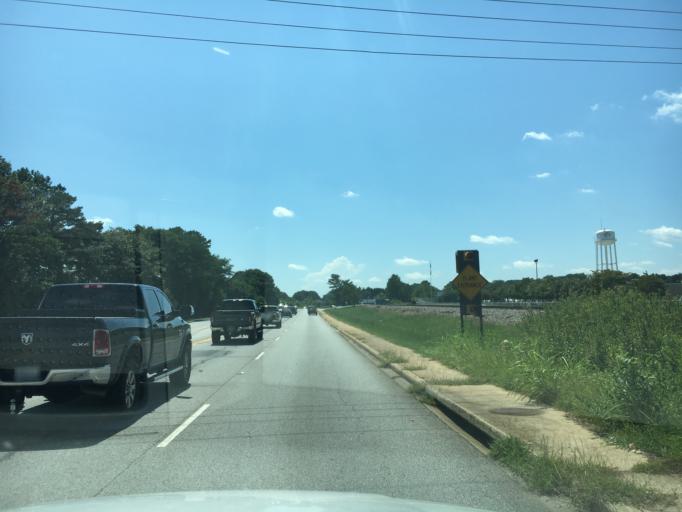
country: US
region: South Carolina
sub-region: Greenville County
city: Wade Hampton
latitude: 34.9013
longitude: -82.3567
